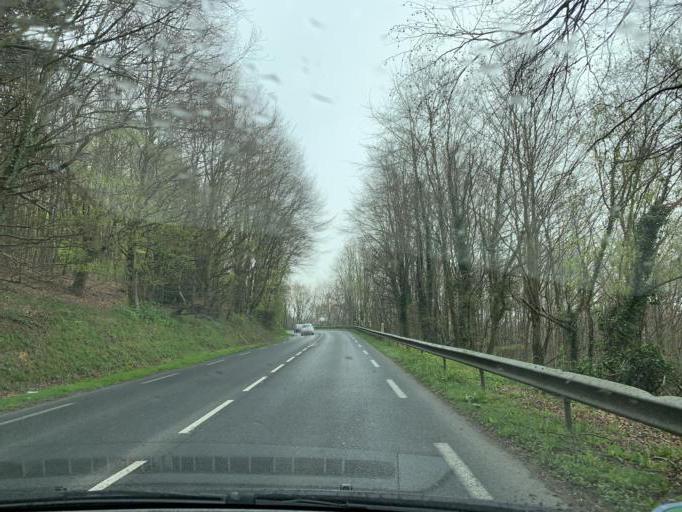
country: FR
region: Haute-Normandie
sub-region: Departement de la Seine-Maritime
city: Cany-Barville
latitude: 49.7857
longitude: 0.6484
